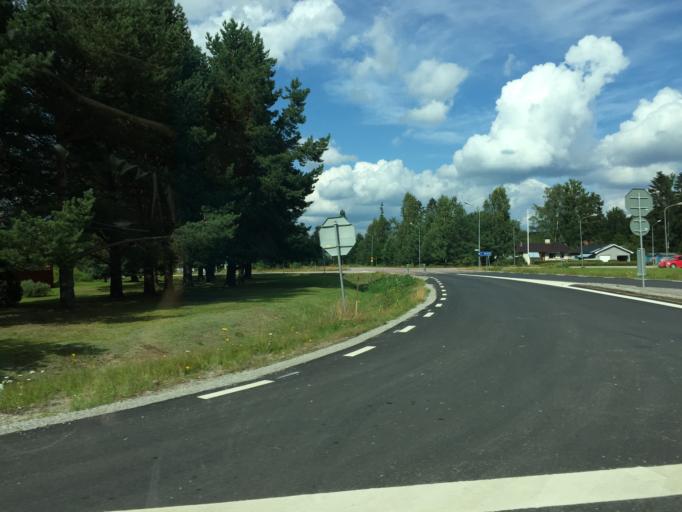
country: SE
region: Gaevleborg
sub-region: Soderhamns Kommun
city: Soderhamn
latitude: 61.1657
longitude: 16.8430
